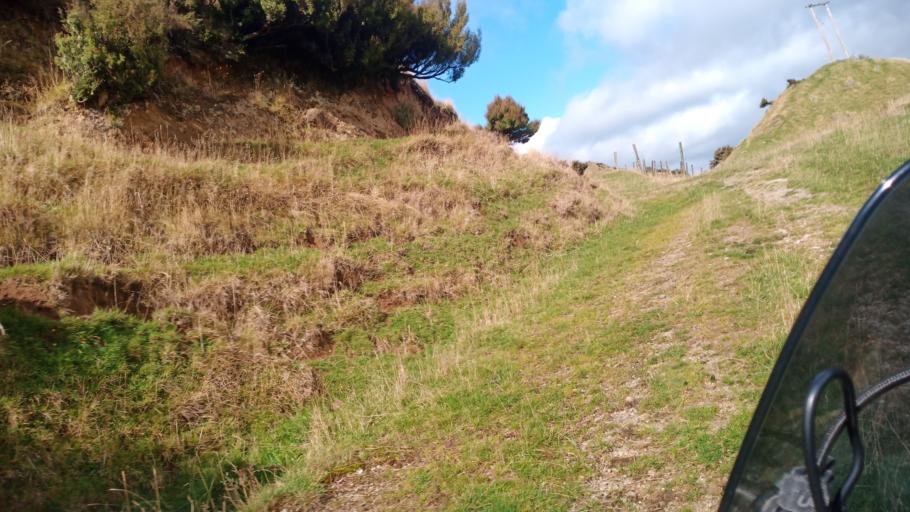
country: NZ
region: Gisborne
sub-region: Gisborne District
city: Gisborne
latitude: -38.4705
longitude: 177.5357
